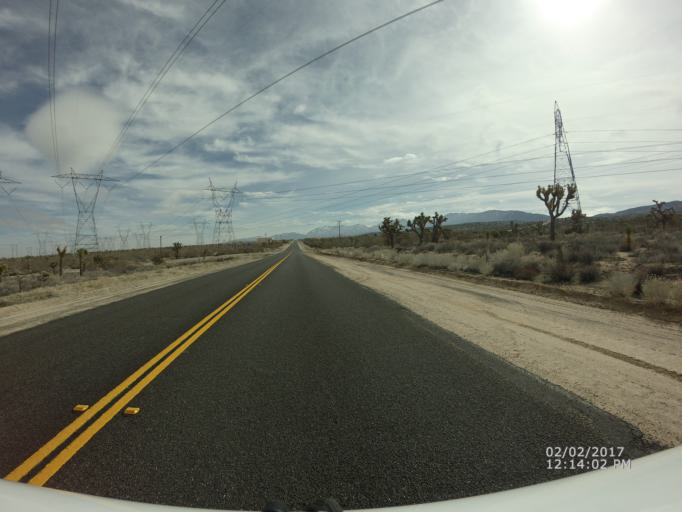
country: US
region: California
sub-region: Los Angeles County
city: Littlerock
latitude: 34.5109
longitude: -117.9759
